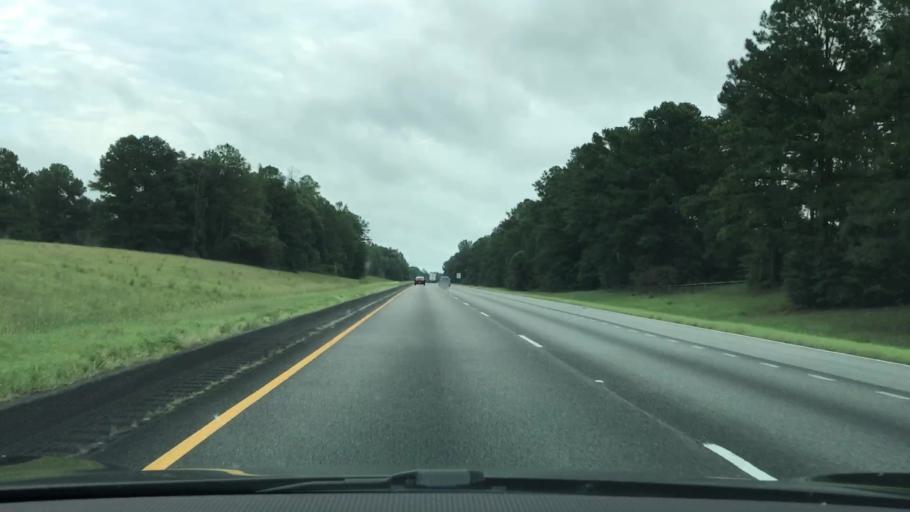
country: US
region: Alabama
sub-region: Elmore County
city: Tallassee
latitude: 32.4333
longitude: -85.8836
